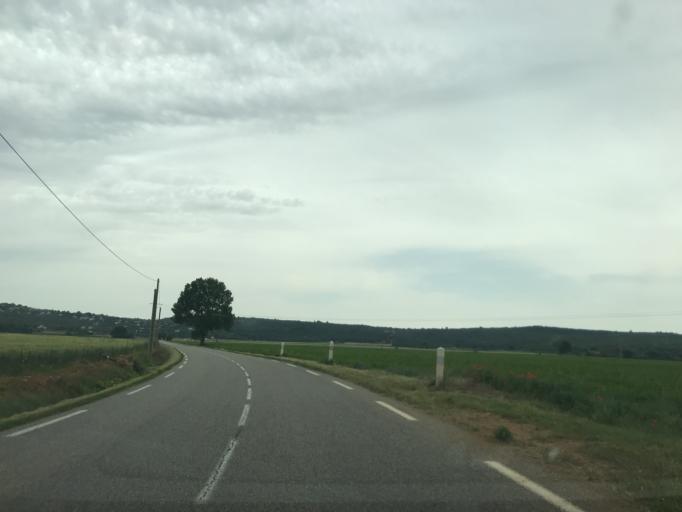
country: FR
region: Provence-Alpes-Cote d'Azur
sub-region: Departement du Var
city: Ginasservis
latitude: 43.6488
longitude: 5.8390
